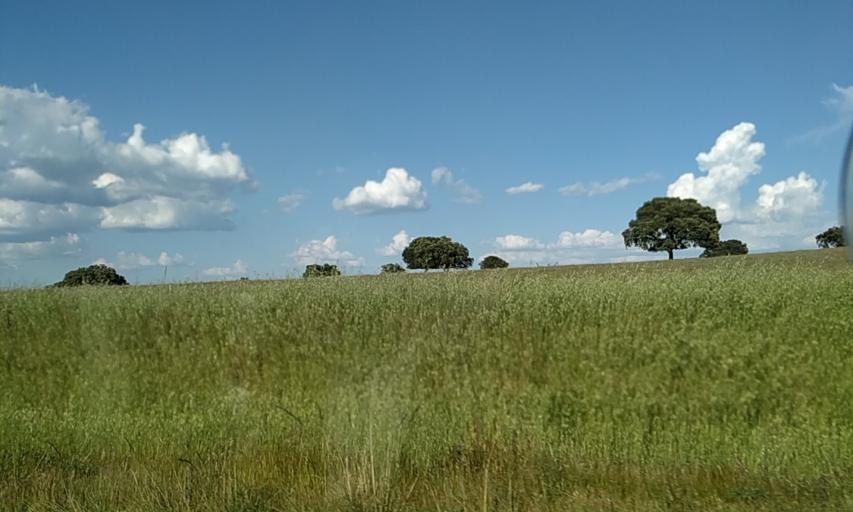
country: PT
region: Portalegre
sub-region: Portalegre
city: Urra
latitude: 39.1121
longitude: -7.4401
